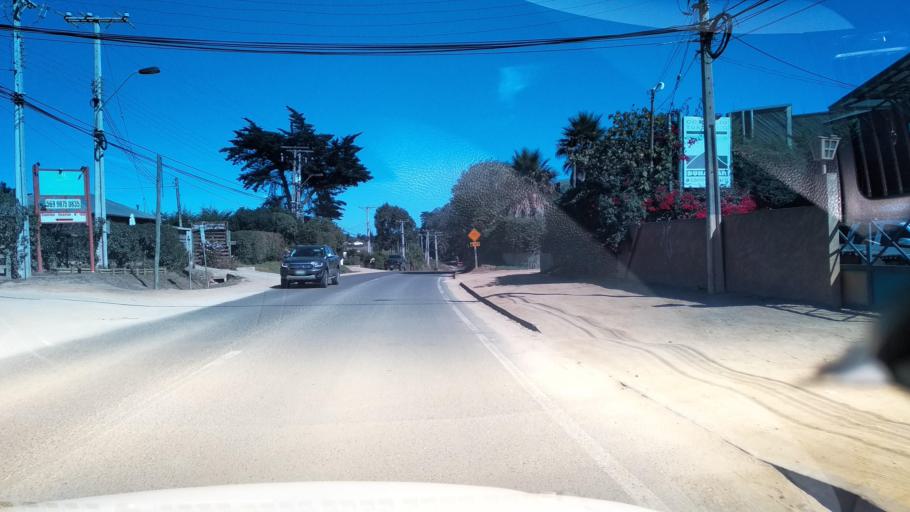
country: CL
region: O'Higgins
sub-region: Provincia de Colchagua
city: Santa Cruz
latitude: -34.4113
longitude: -72.0274
